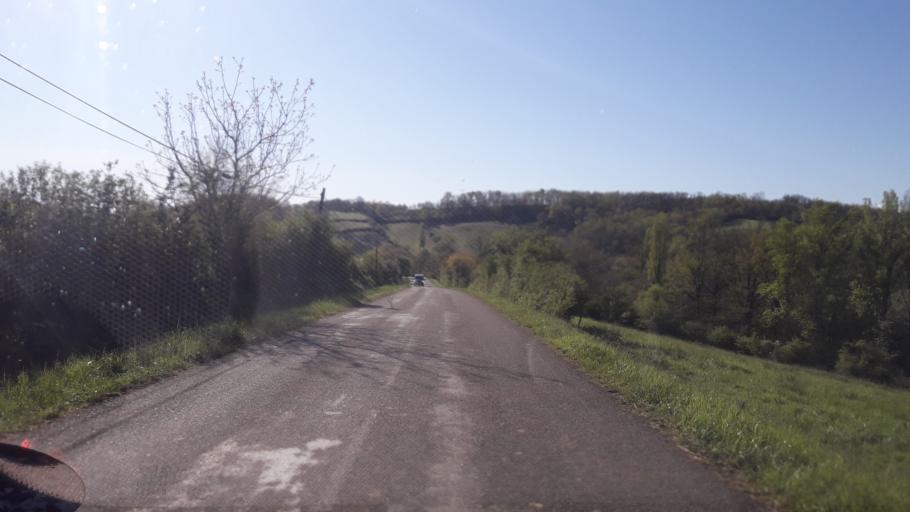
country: FR
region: Midi-Pyrenees
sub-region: Departement de la Haute-Garonne
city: Cazeres
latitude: 43.1950
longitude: 1.1397
